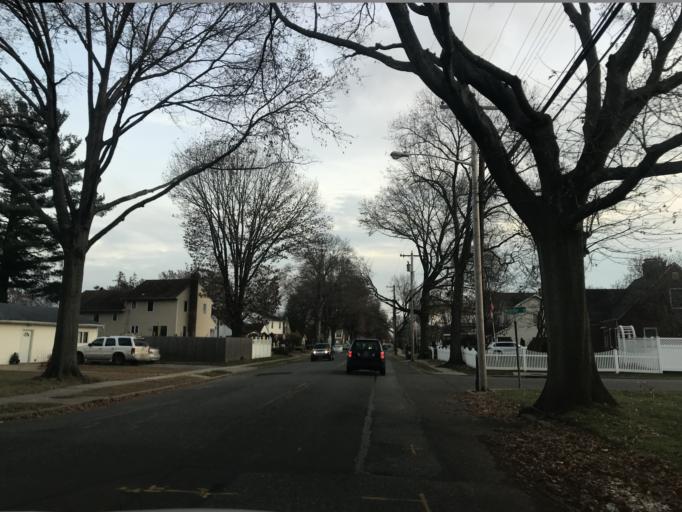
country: US
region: New York
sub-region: Nassau County
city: Carle Place
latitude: 40.7575
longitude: -73.5996
